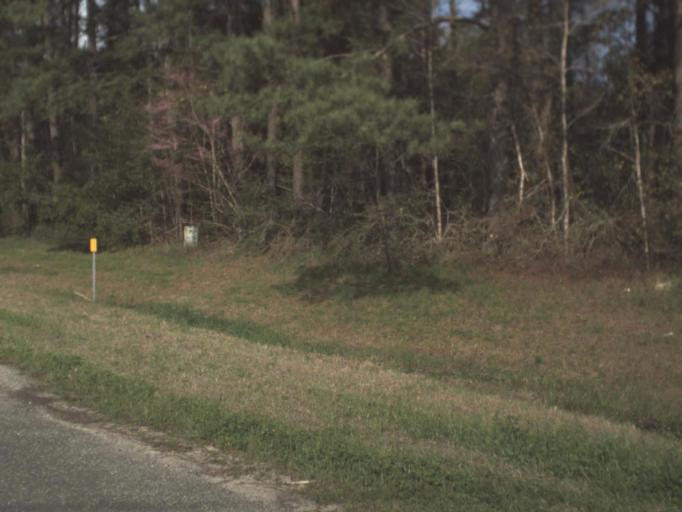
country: US
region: Florida
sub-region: Jefferson County
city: Monticello
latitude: 30.4986
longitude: -83.8796
